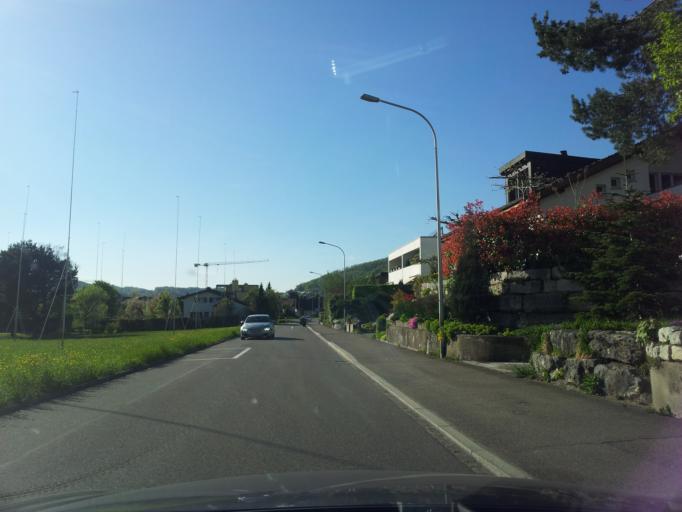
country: CH
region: Aargau
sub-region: Bezirk Baden
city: Neuenhof
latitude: 47.4632
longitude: 8.3371
